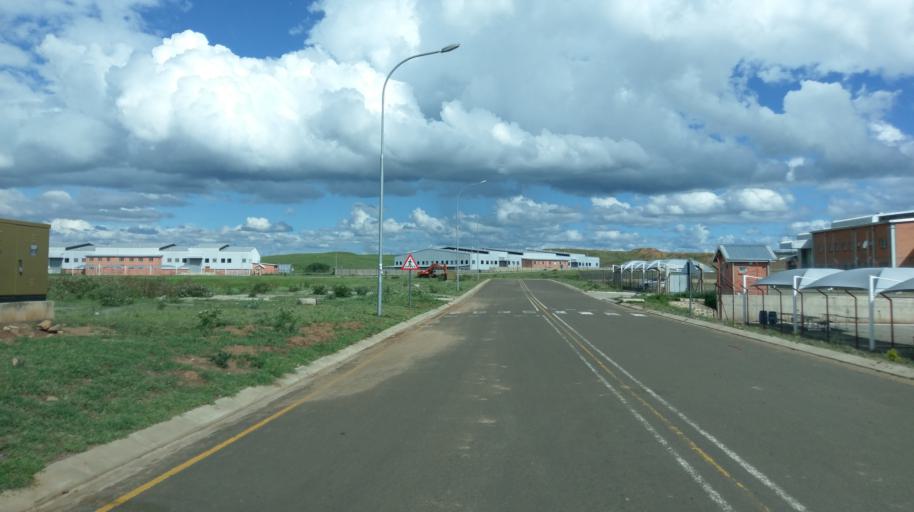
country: LS
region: Maseru
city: Maseru
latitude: -29.3821
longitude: 27.4844
